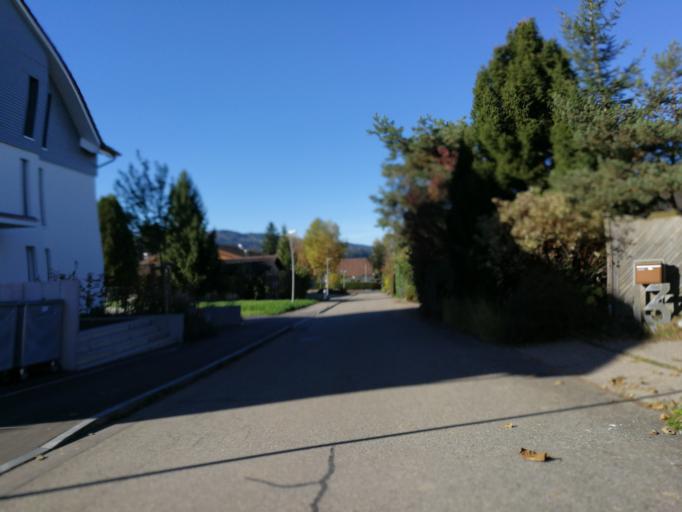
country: CH
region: Zurich
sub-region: Bezirk Meilen
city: Oetwil am See
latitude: 47.2731
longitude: 8.7248
